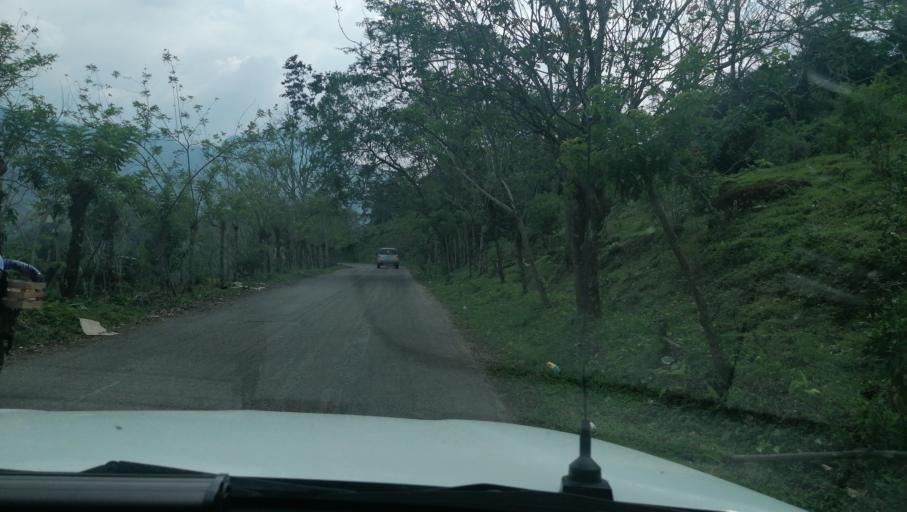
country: MX
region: Chiapas
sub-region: Francisco Leon
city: San Miguel la Sardina
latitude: 17.2269
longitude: -93.3448
